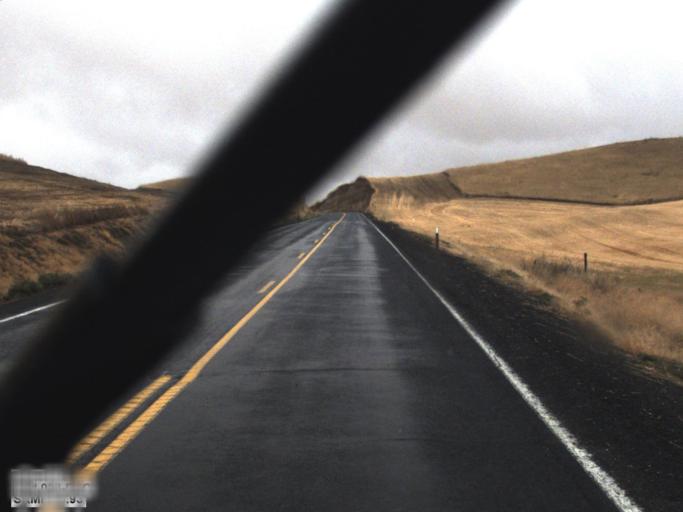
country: US
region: Washington
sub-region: Spokane County
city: Cheney
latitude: 47.1564
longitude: -117.8626
